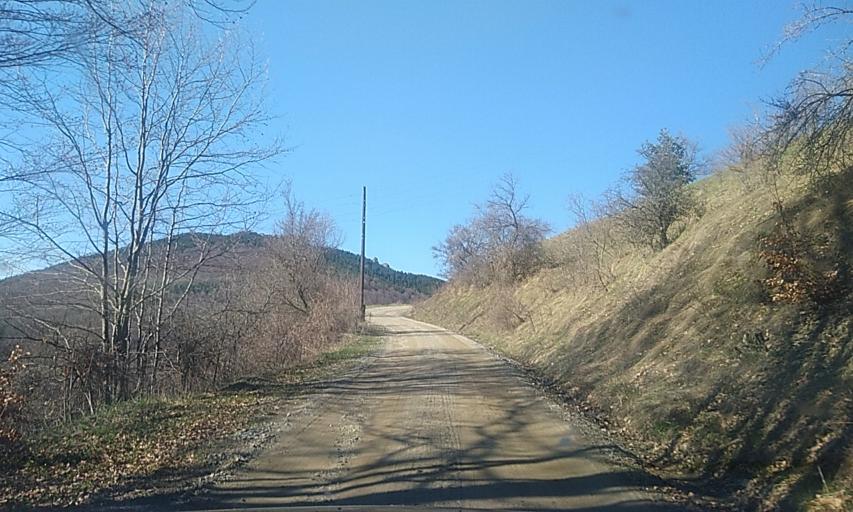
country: MK
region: Kriva Palanka
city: Kriva Palanka
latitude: 42.3452
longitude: 22.3482
